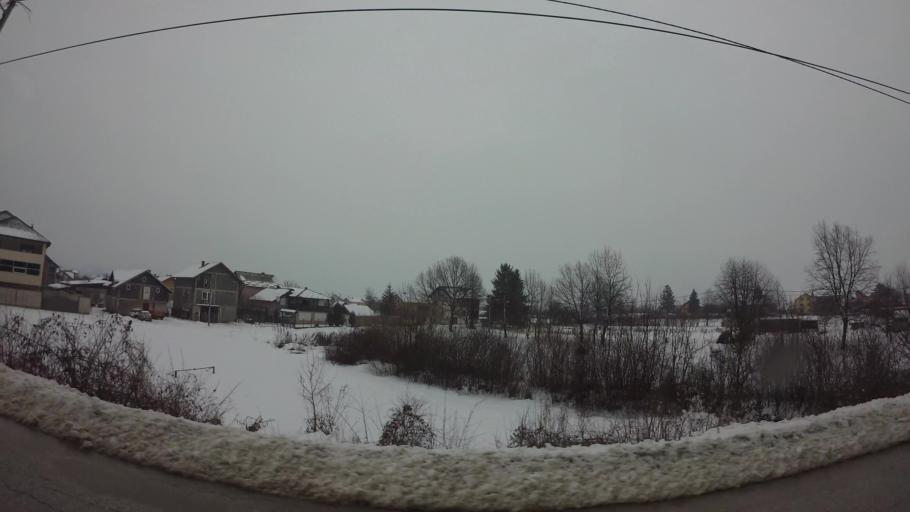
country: BA
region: Federation of Bosnia and Herzegovina
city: Hadzici
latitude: 43.8517
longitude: 18.2765
